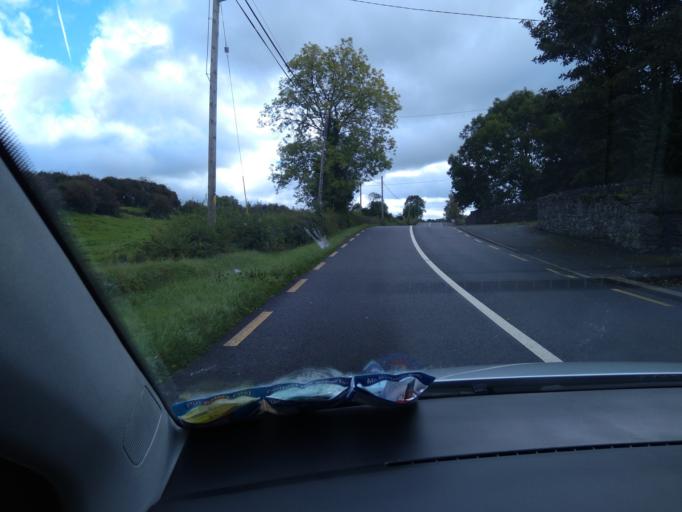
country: IE
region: Connaught
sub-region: Sligo
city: Collooney
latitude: 54.1966
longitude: -8.4509
